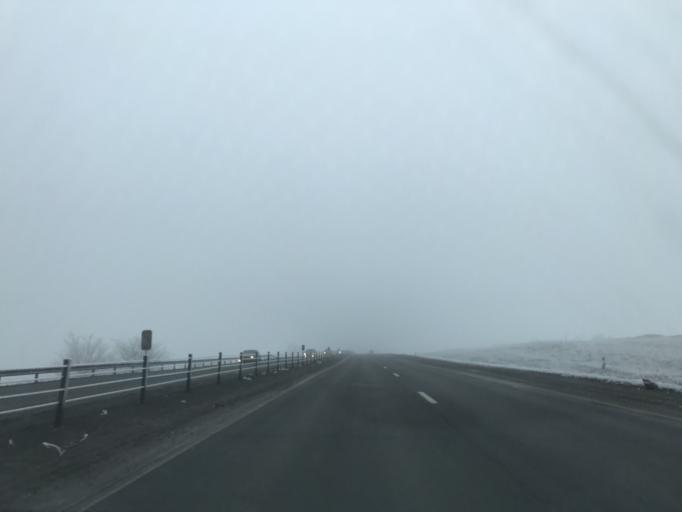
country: RU
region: Rostov
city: Likhoy
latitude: 48.1589
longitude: 40.2621
